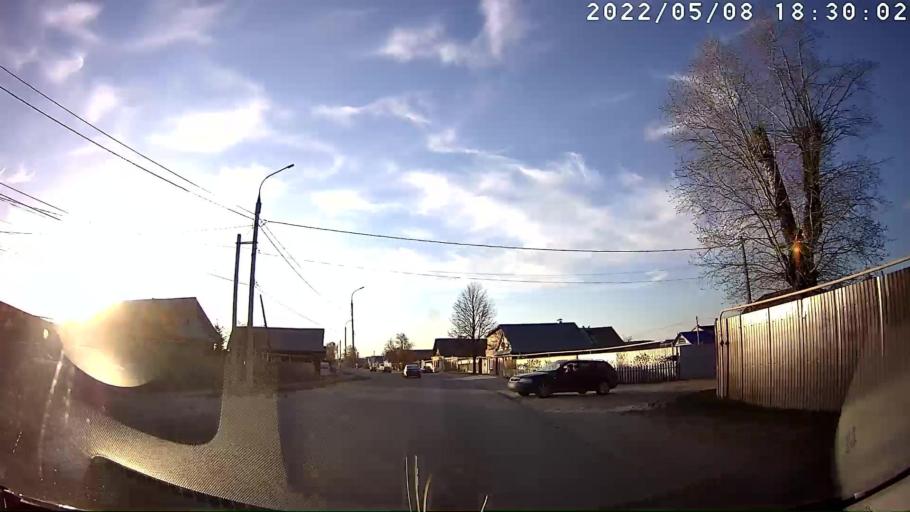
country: RU
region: Mariy-El
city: Volzhsk
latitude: 55.8710
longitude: 48.3676
